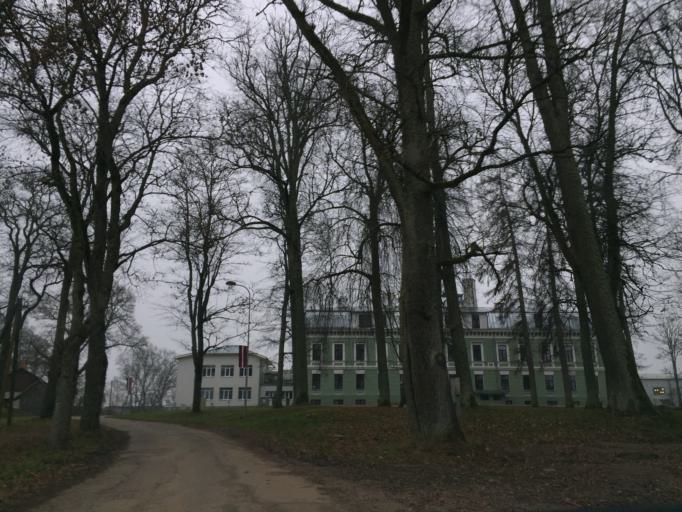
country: LV
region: Koceni
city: Koceni
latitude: 57.5235
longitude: 25.3333
